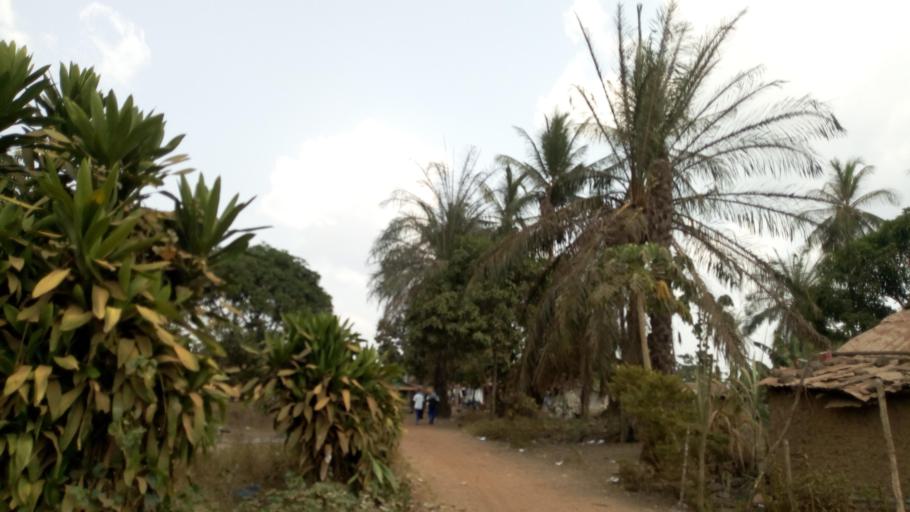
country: SL
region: Southern Province
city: Mogbwemo
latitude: 7.7885
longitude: -12.2988
